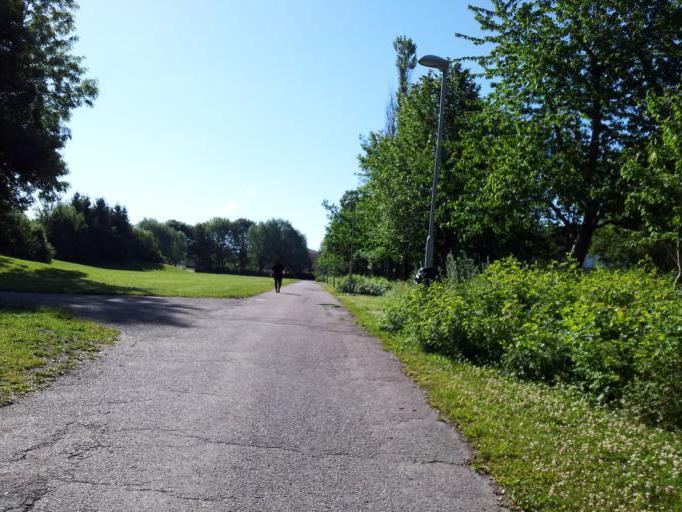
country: SE
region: Uppsala
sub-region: Uppsala Kommun
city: Uppsala
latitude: 59.8746
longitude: 17.6606
